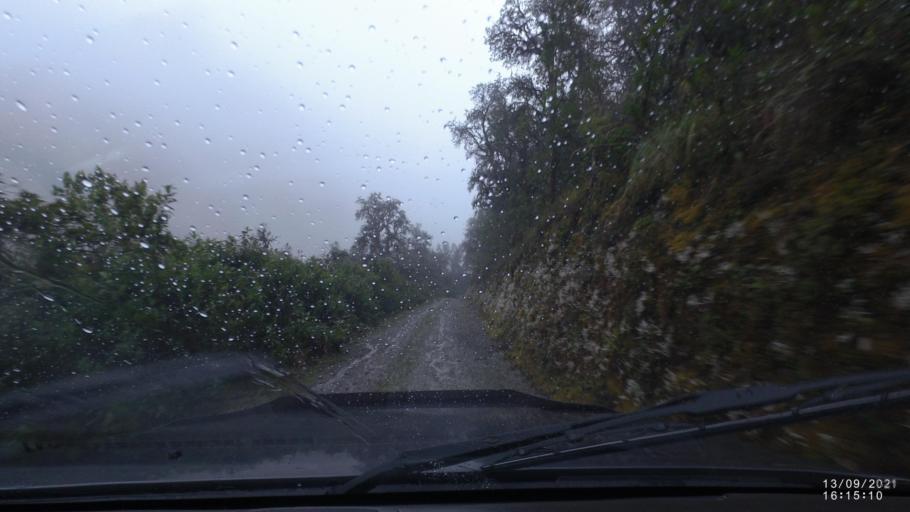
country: BO
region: Cochabamba
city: Colomi
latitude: -17.2757
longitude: -65.7119
